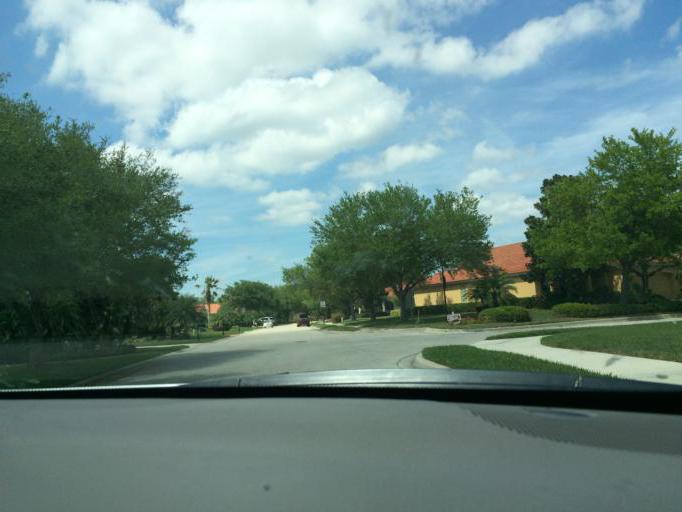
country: US
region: Florida
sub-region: Manatee County
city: Ellenton
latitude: 27.5075
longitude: -82.4467
